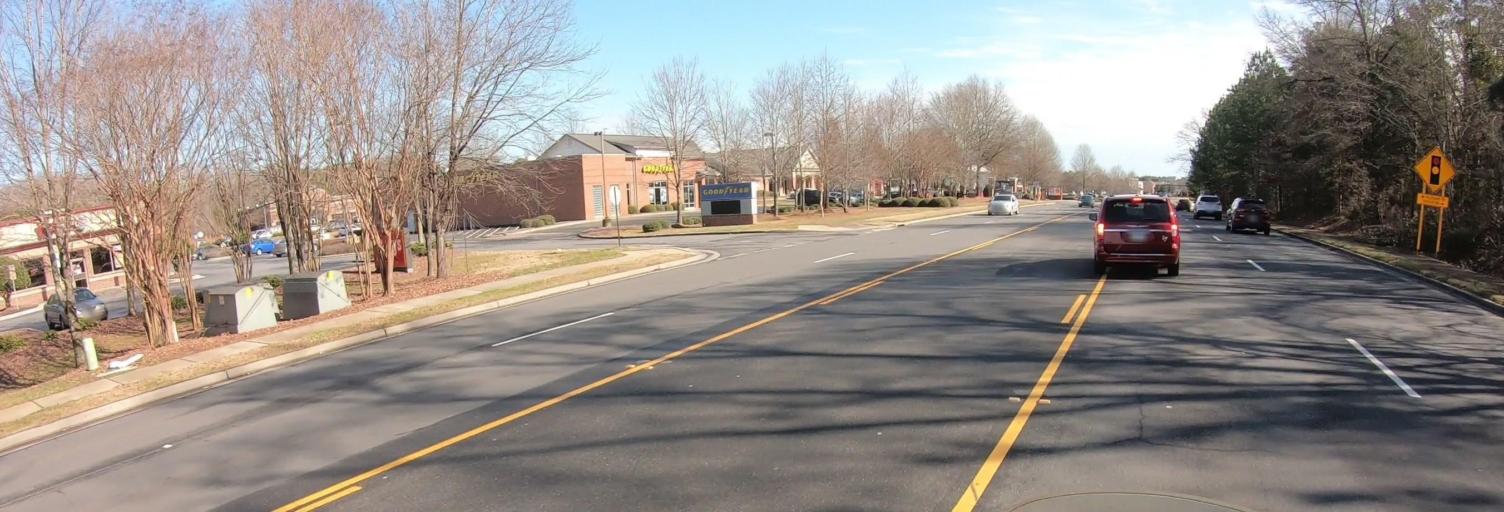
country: US
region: South Carolina
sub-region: York County
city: Fort Mill
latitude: 35.0345
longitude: -80.9732
